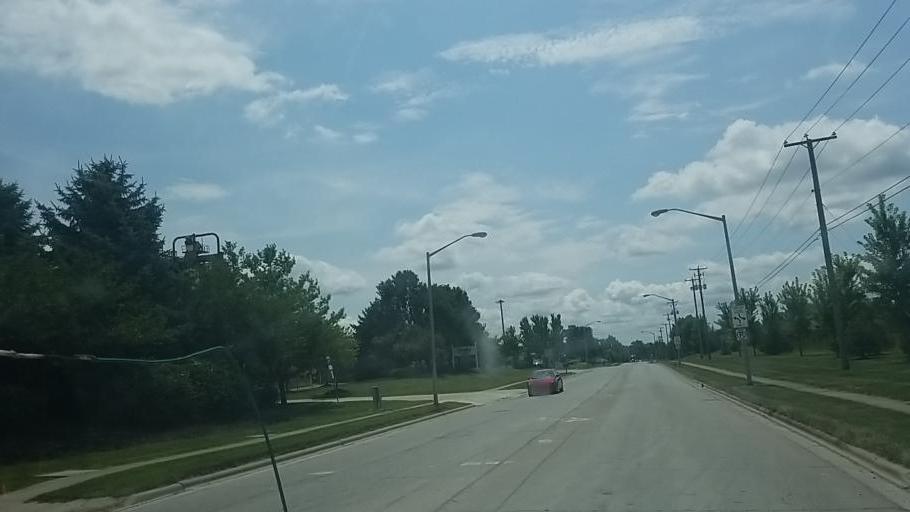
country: US
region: Ohio
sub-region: Franklin County
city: Reynoldsburg
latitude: 39.9804
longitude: -82.7686
